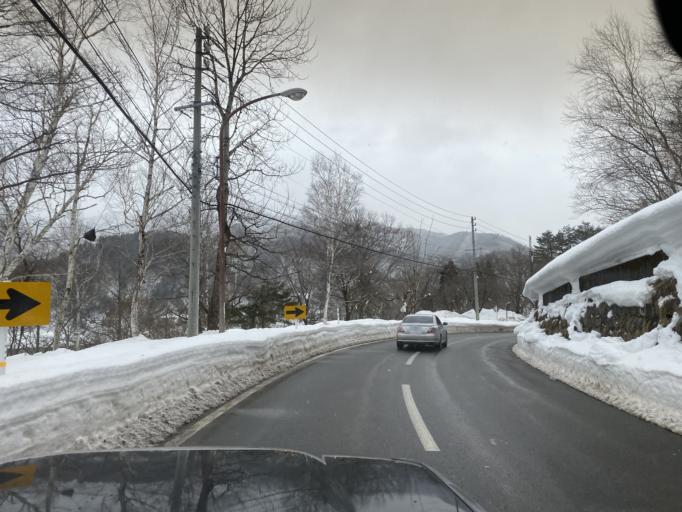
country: JP
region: Gifu
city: Takayama
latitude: 36.0990
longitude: 136.9334
